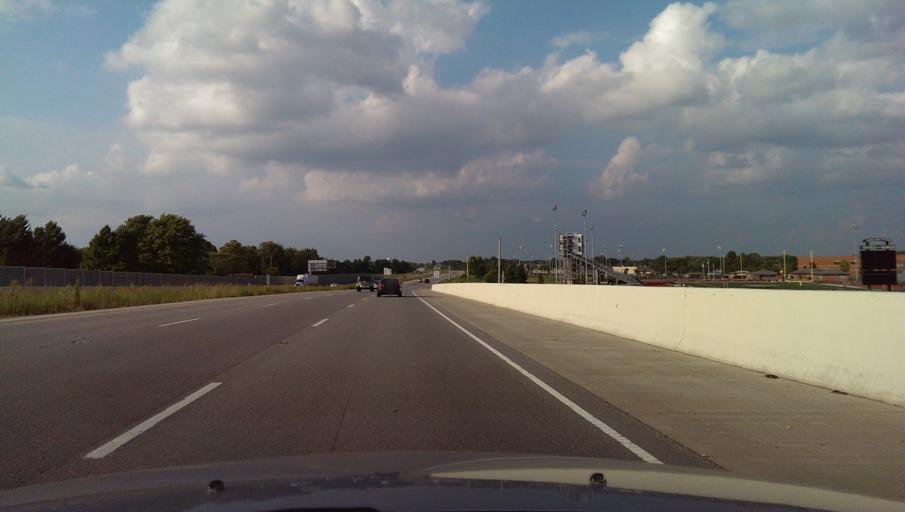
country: US
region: Indiana
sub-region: Hamilton County
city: Westfield
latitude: 40.0510
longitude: -86.1339
